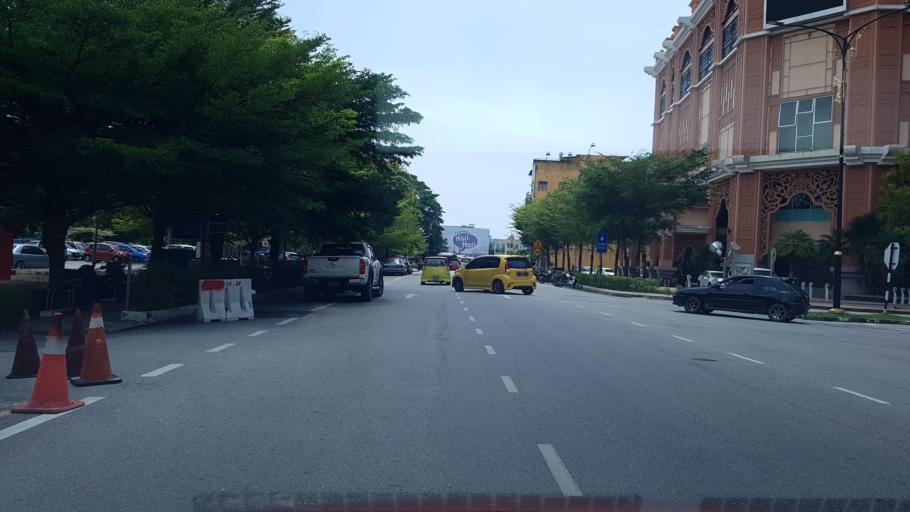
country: MY
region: Terengganu
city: Kuala Terengganu
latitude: 5.3306
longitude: 103.1361
